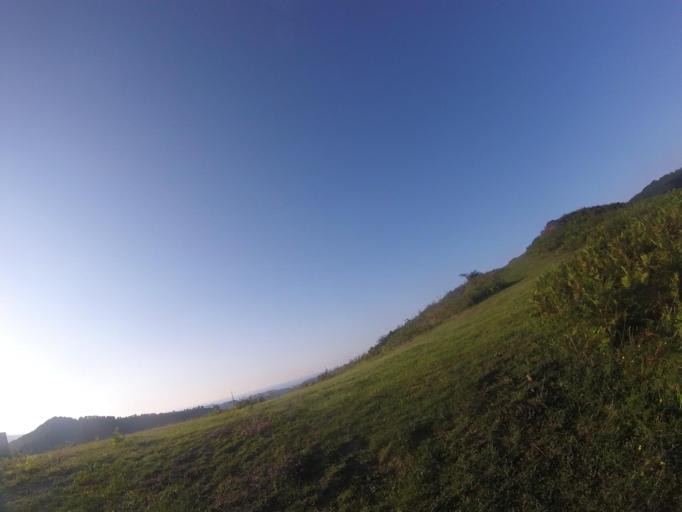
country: ES
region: Navarre
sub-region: Provincia de Navarra
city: Arano
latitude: 43.2503
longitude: -1.8929
